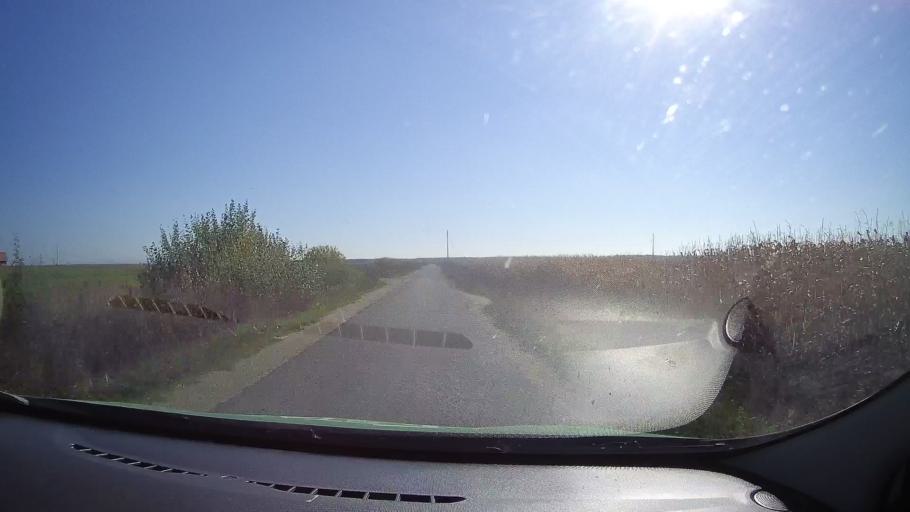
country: RO
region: Satu Mare
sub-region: Comuna Doba
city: Doba
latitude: 47.7378
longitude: 22.7192
